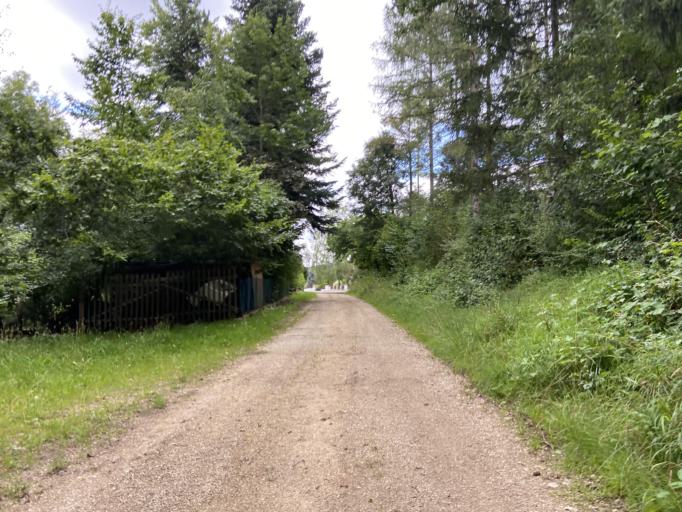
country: DE
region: Baden-Wuerttemberg
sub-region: Tuebingen Region
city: Bingen
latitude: 48.1018
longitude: 9.2908
